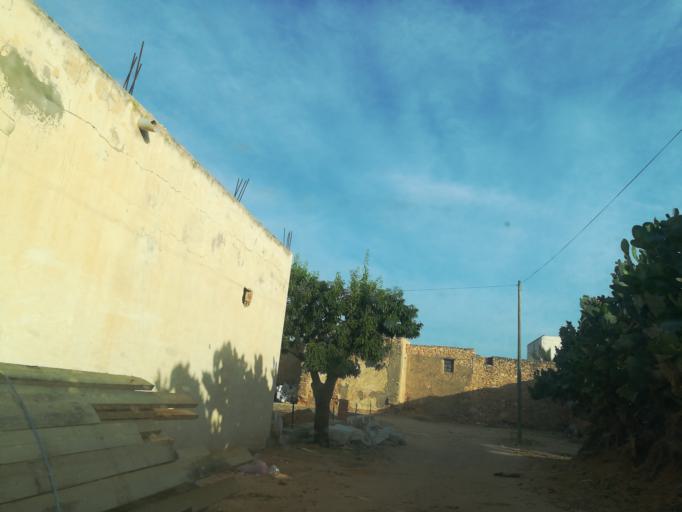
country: TN
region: Safaqis
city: Al Qarmadah
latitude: 34.8149
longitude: 10.7503
